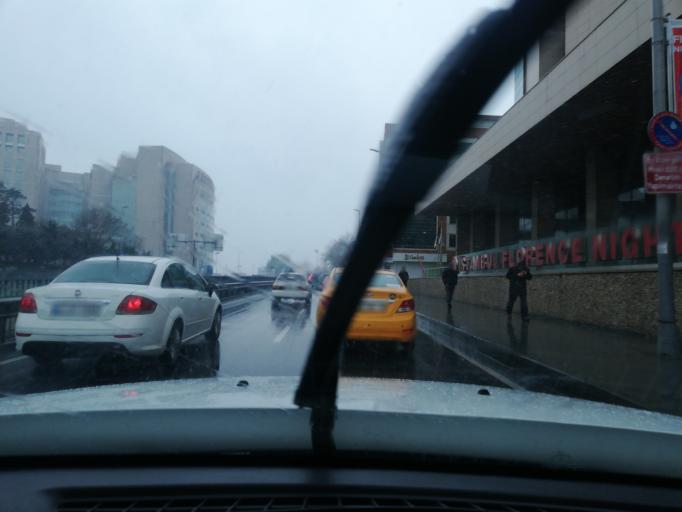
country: TR
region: Istanbul
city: Sisli
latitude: 41.0688
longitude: 28.9833
